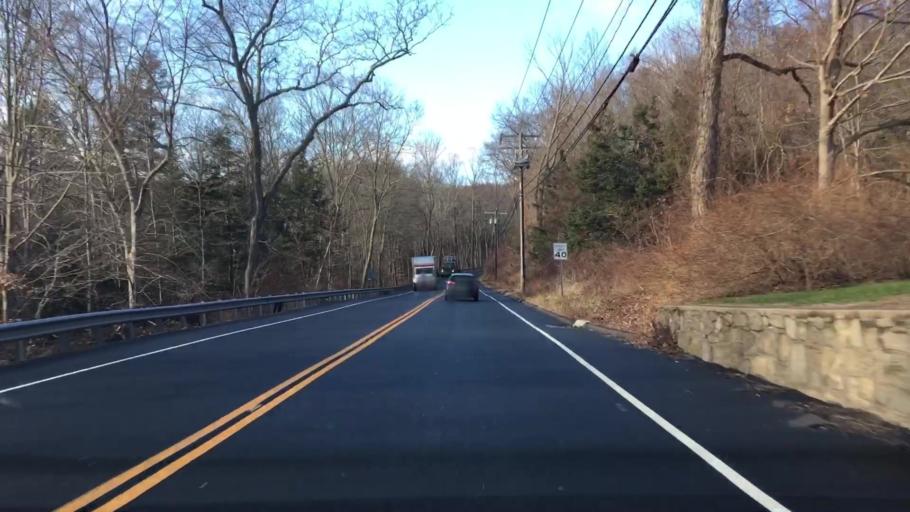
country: US
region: Connecticut
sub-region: New Haven County
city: Oxford
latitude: 41.3893
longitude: -73.1927
